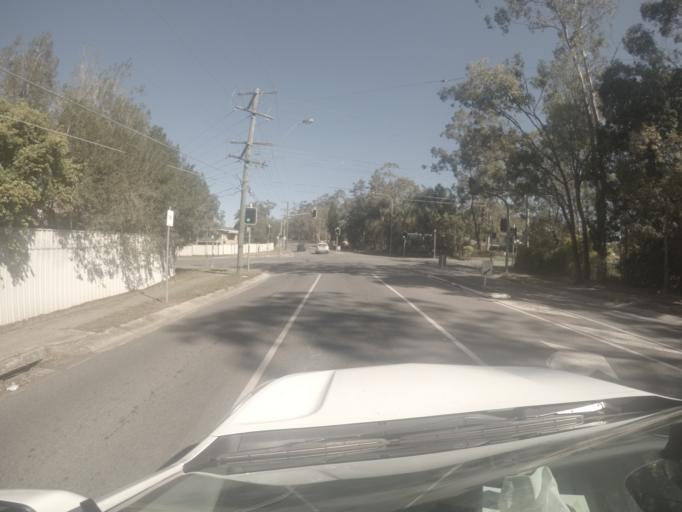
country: AU
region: Queensland
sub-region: Ipswich
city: Springfield
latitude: -27.6322
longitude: 152.9158
